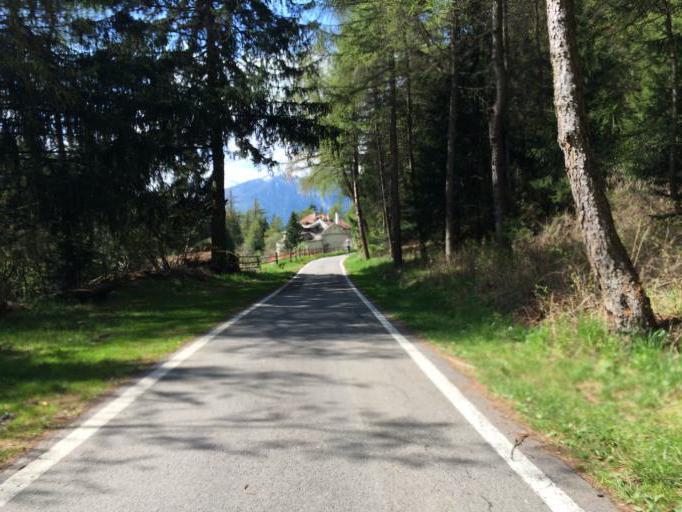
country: IT
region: Trentino-Alto Adige
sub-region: Bolzano
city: Malles Venosta
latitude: 46.7358
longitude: 10.5329
